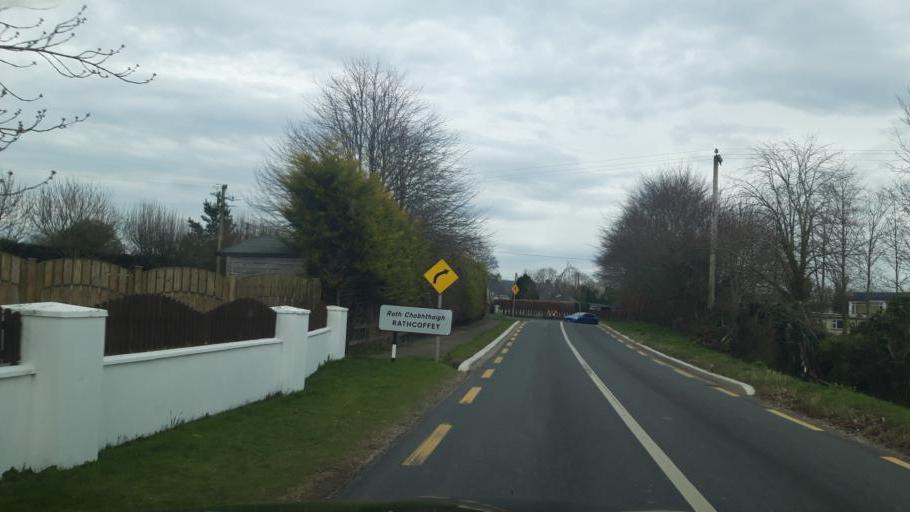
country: IE
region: Leinster
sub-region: Kildare
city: Clane
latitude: 53.3336
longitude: -6.6801
